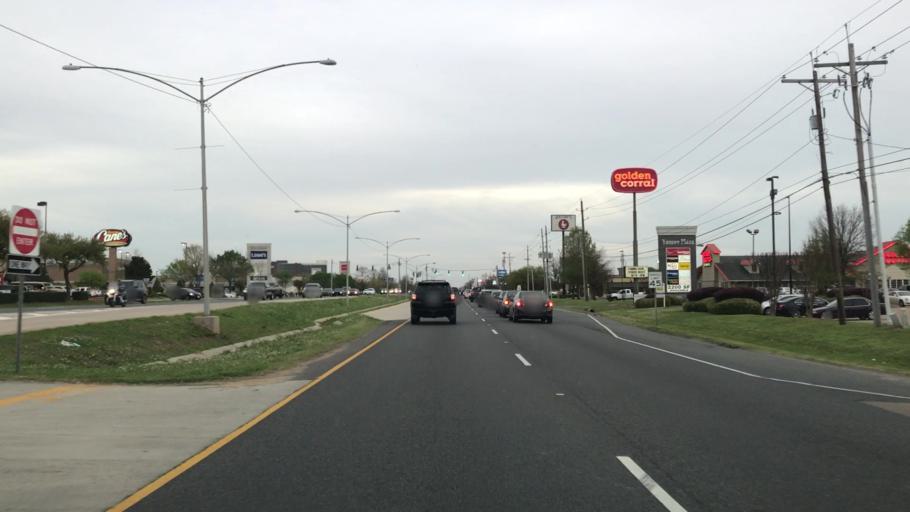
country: US
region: Louisiana
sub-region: Bossier Parish
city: Bossier City
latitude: 32.4401
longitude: -93.7168
